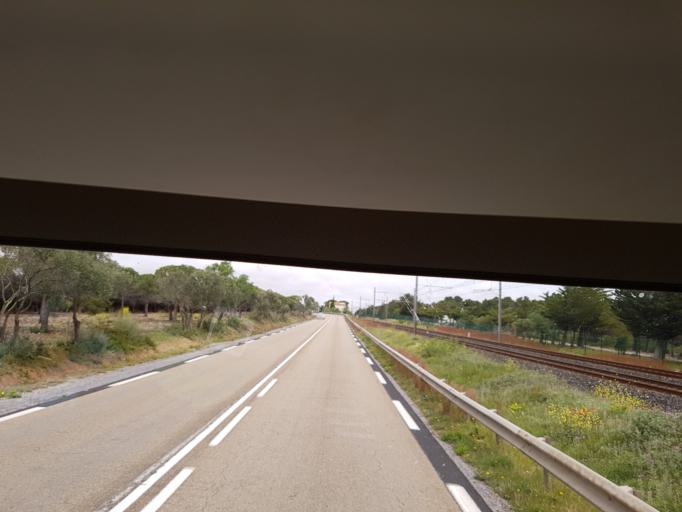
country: FR
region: Languedoc-Roussillon
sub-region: Departement de l'Aude
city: Leucate
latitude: 42.8757
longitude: 2.9926
